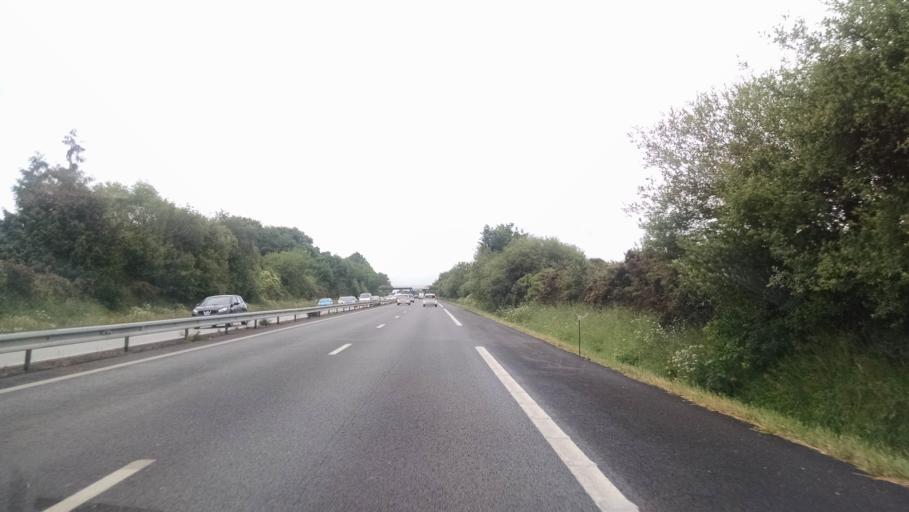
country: FR
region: Brittany
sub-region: Departement du Morbihan
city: Nostang
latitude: 47.7717
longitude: -3.1784
